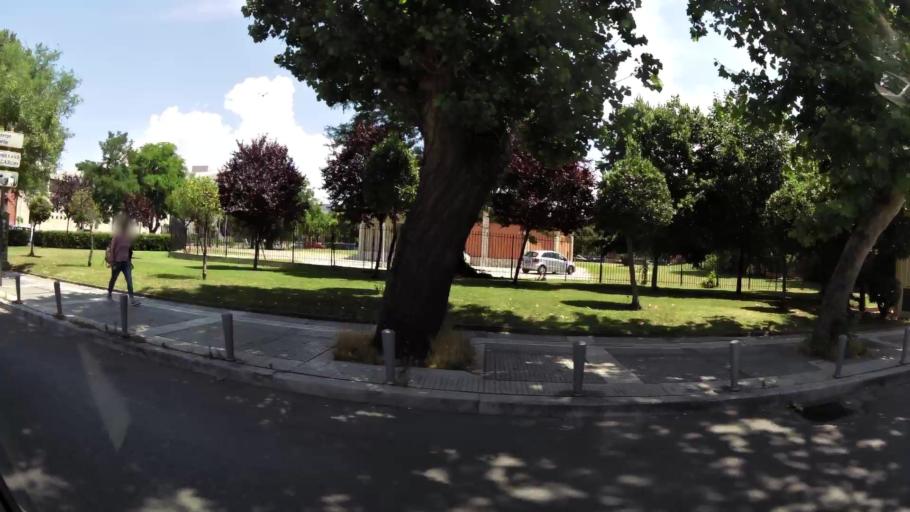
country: GR
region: Central Macedonia
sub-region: Nomos Thessalonikis
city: Agios Pavlos
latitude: 40.6224
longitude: 22.9535
